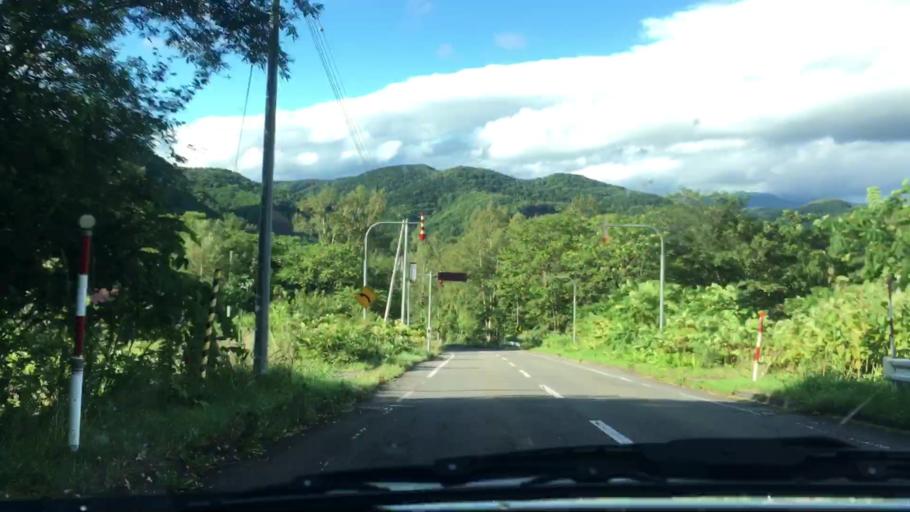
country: JP
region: Hokkaido
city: Otofuke
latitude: 43.1811
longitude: 142.9293
